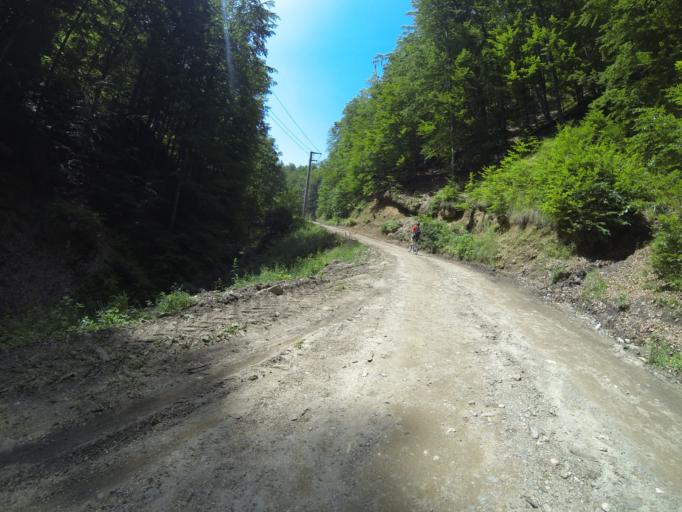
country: RO
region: Valcea
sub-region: Oras Baile Olanesti
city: Baile Olanesti
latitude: 45.2101
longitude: 24.2154
